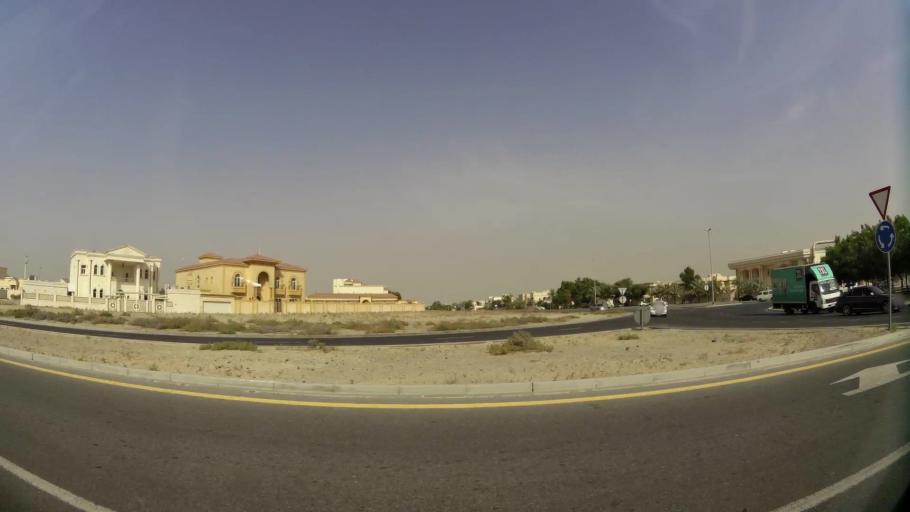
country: AE
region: Ash Shariqah
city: Sharjah
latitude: 25.2579
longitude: 55.4560
